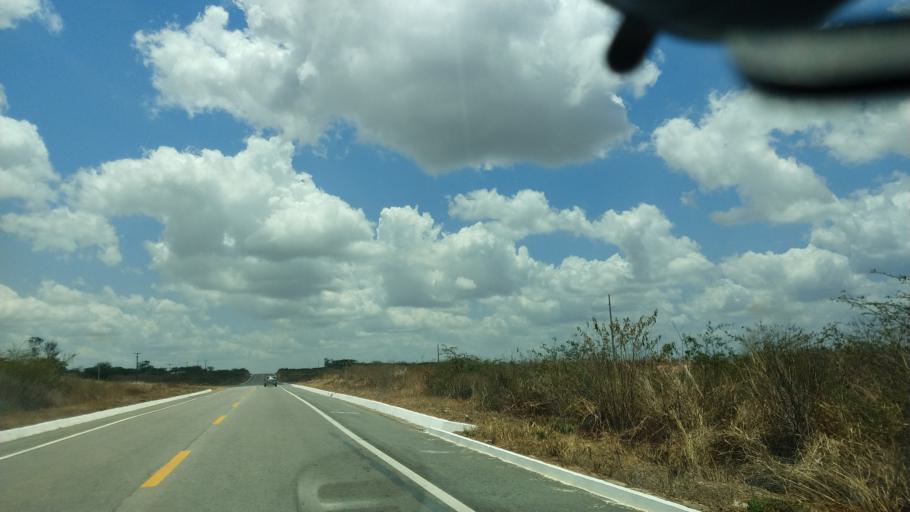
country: BR
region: Rio Grande do Norte
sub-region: Cerro Cora
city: Cerro Cora
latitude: -6.1907
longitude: -36.2234
